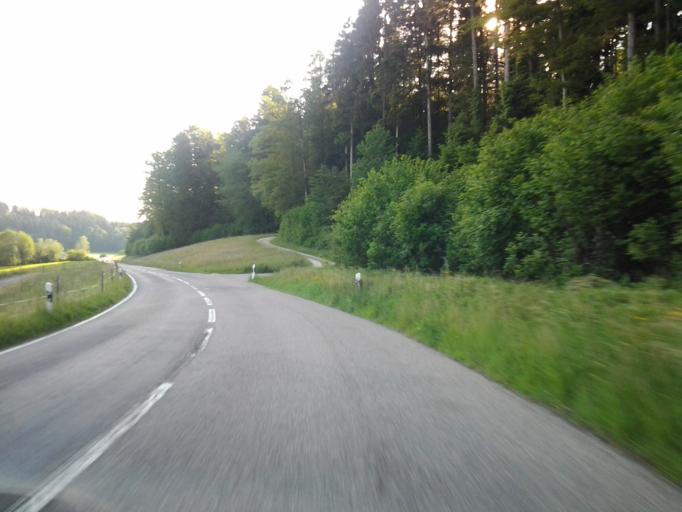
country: CH
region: Lucerne
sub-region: Willisau District
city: Pfaffnau
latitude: 47.2212
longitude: 7.8672
